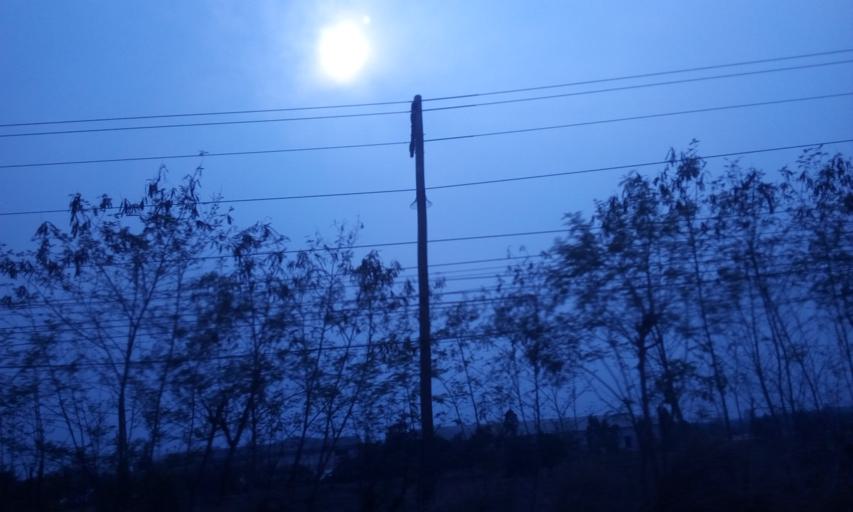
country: TH
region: Chachoengsao
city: Plaeng Yao
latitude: 13.5316
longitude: 101.2628
